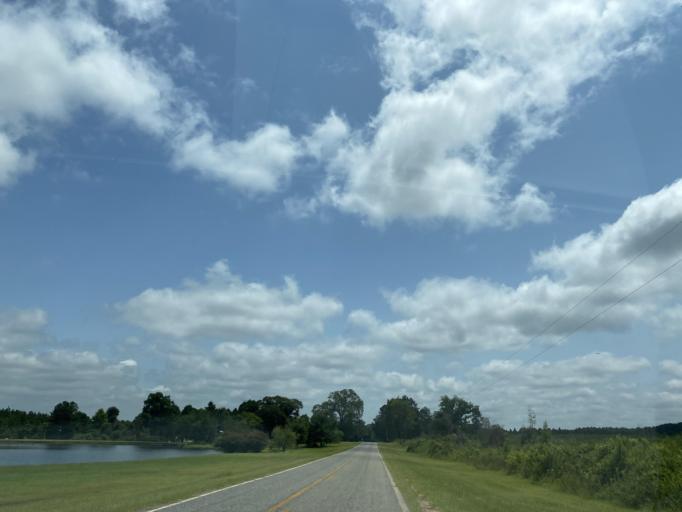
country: US
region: Georgia
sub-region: Wheeler County
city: Alamo
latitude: 32.0819
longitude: -82.7554
